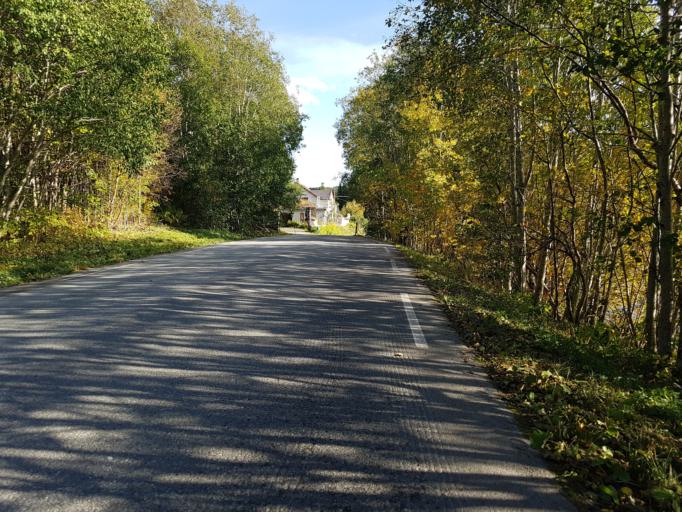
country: NO
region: Sor-Trondelag
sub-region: Malvik
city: Malvik
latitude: 63.3832
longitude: 10.5950
